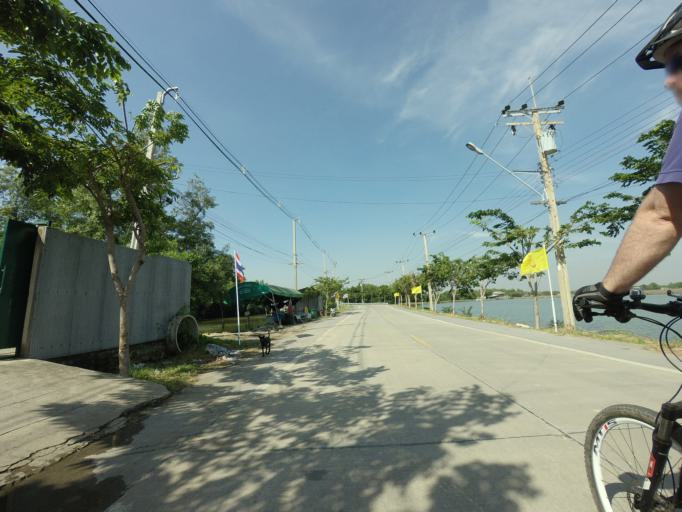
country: TH
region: Samut Prakan
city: Phra Samut Chedi
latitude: 13.5439
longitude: 100.5153
